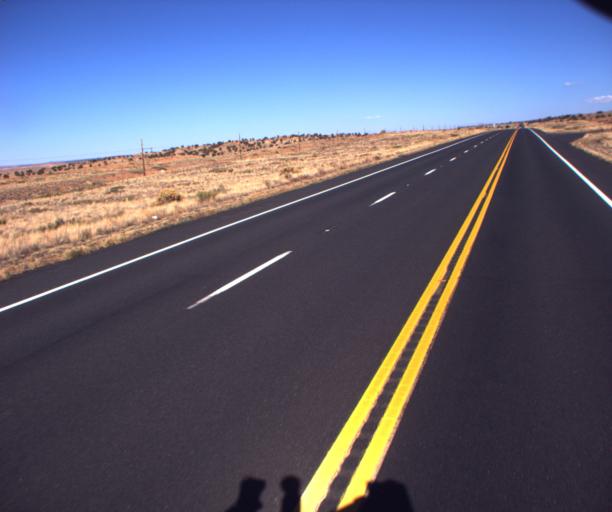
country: US
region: Arizona
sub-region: Coconino County
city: Kaibito
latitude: 36.4321
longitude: -110.7710
